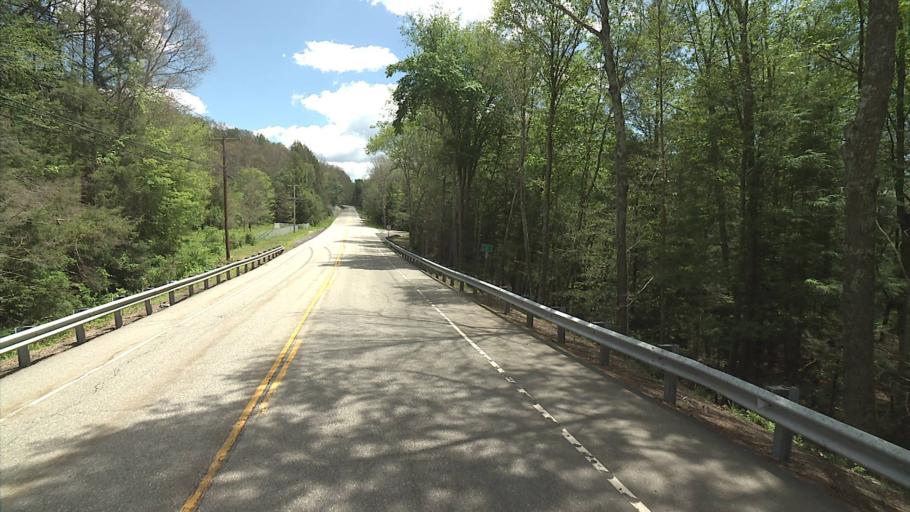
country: US
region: Connecticut
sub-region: Middlesex County
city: Moodus
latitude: 41.5165
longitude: -72.4995
